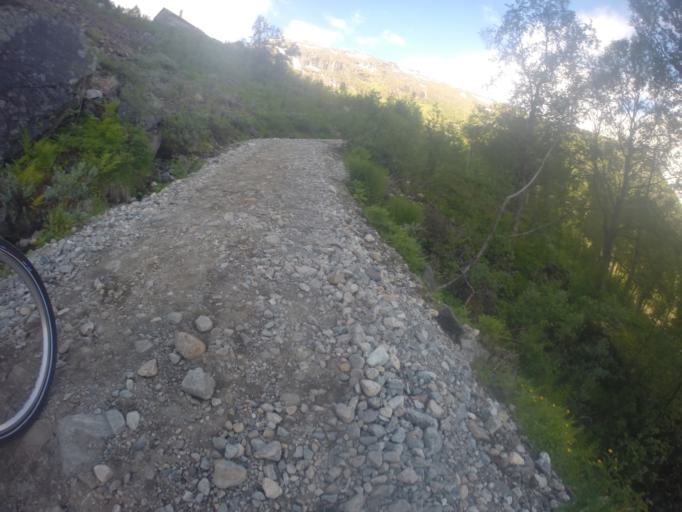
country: NO
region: Sogn og Fjordane
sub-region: Aurland
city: Aurlandsvangen
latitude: 60.7402
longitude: 7.1243
